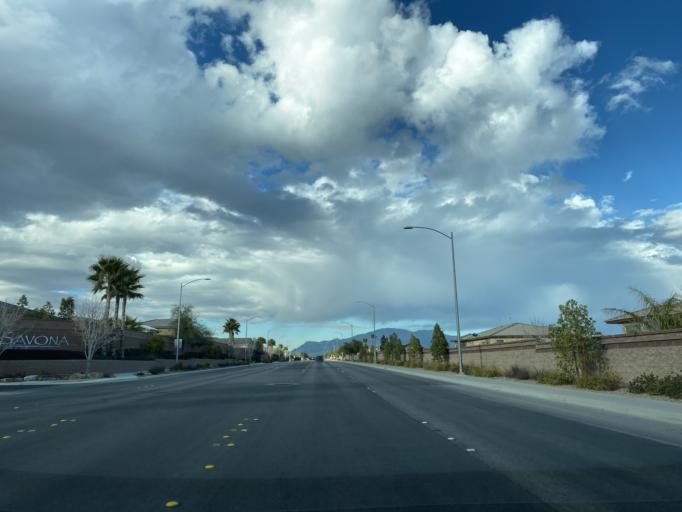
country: US
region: Nevada
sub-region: Clark County
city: Summerlin South
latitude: 36.2890
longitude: -115.3059
